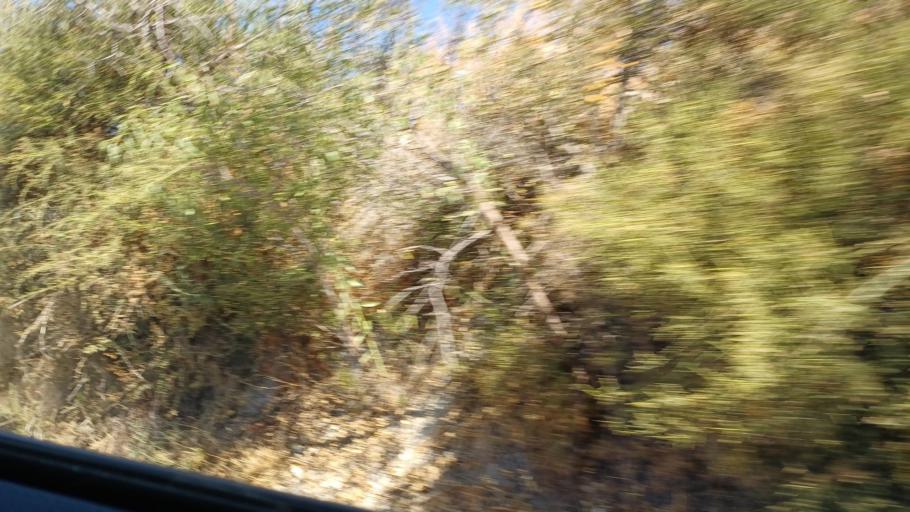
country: CY
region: Pafos
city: Mesogi
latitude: 34.9218
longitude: 32.5725
